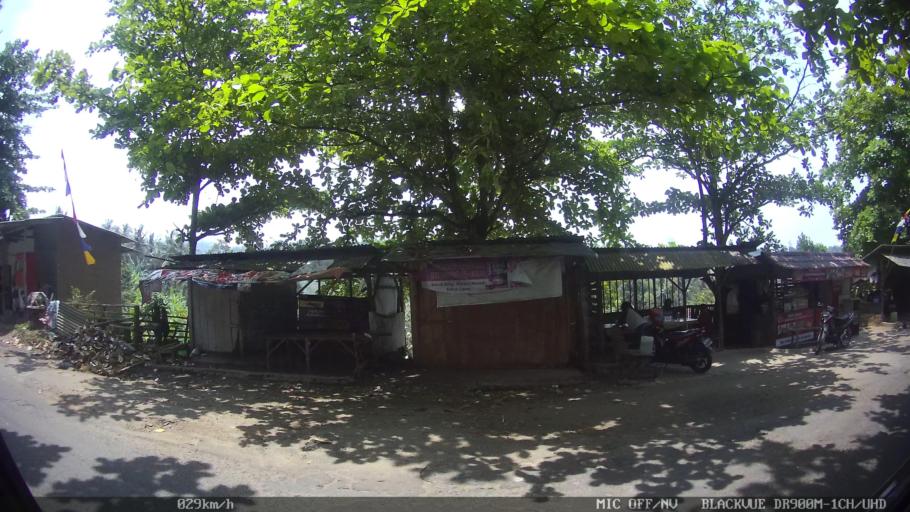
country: ID
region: Lampung
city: Bandarlampung
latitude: -5.4378
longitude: 105.2423
